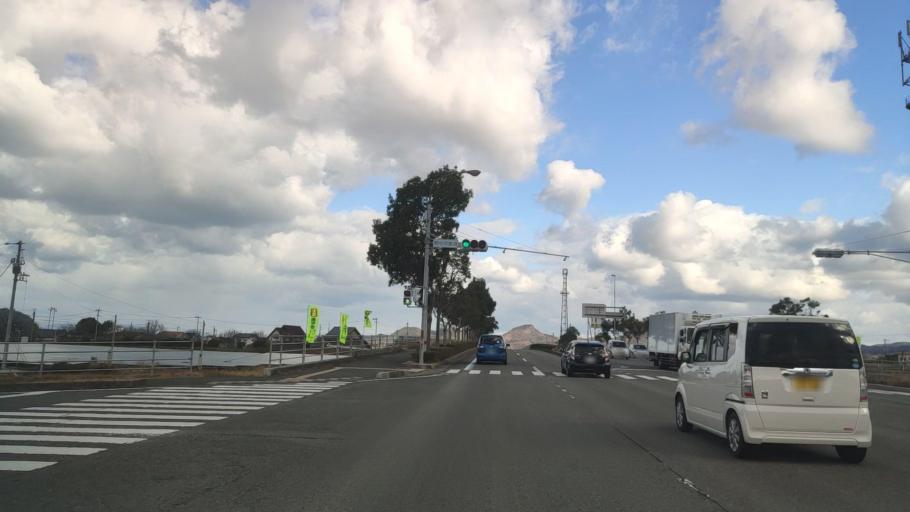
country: JP
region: Ehime
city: Hojo
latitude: 33.9534
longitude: 132.7752
